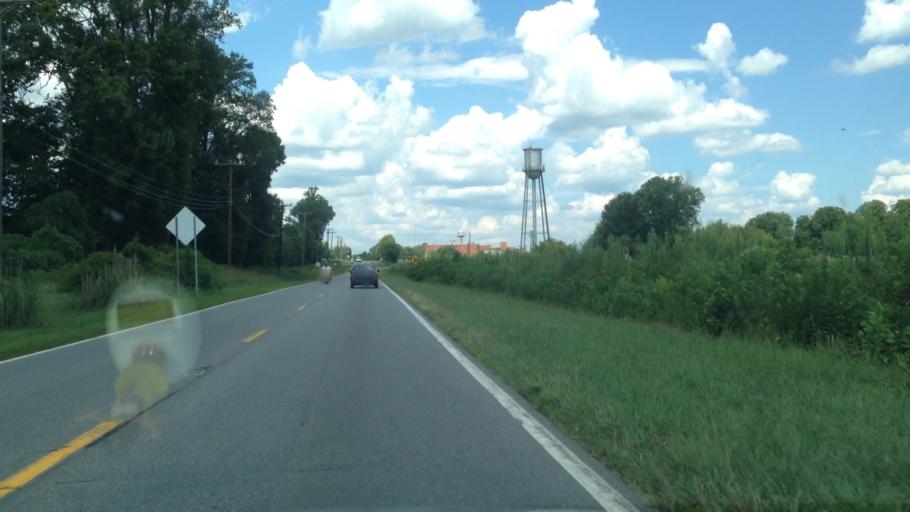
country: US
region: North Carolina
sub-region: Rockingham County
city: Reidsville
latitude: 36.3861
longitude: -79.6499
